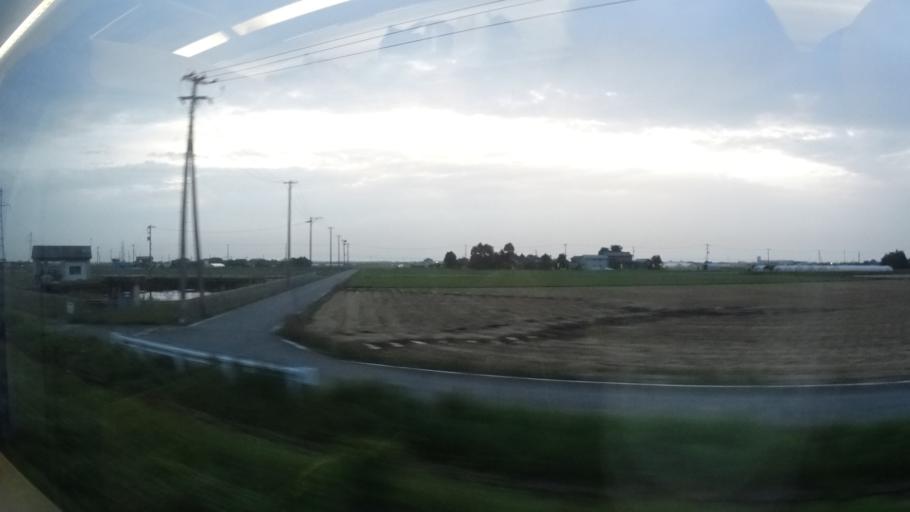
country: JP
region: Niigata
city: Shibata
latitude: 38.0412
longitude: 139.3922
